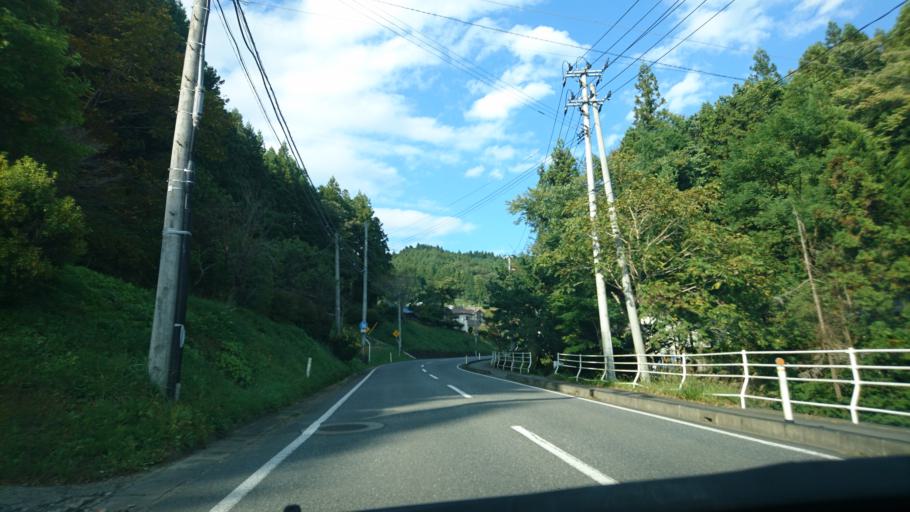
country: JP
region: Iwate
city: Ichinoseki
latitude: 38.8584
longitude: 141.3412
